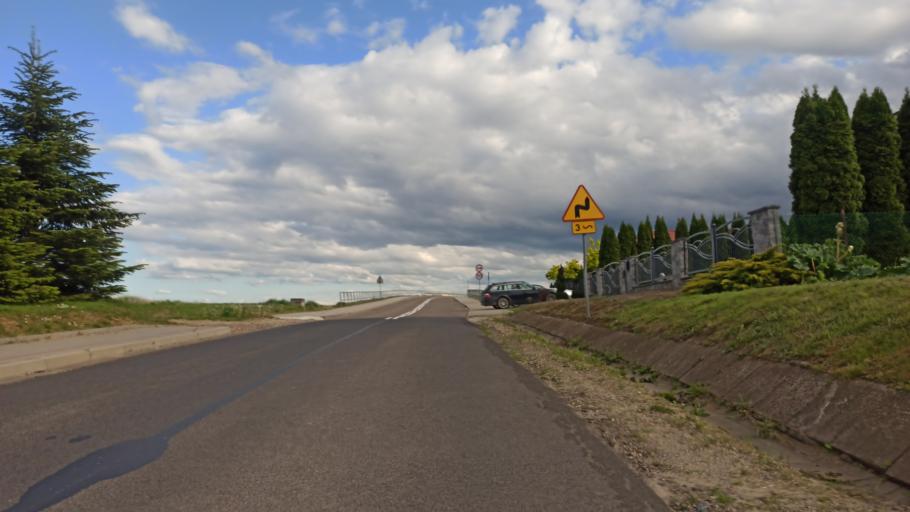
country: PL
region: Subcarpathian Voivodeship
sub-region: Powiat jaroslawski
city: Sosnica
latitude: 49.9176
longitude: 22.8589
